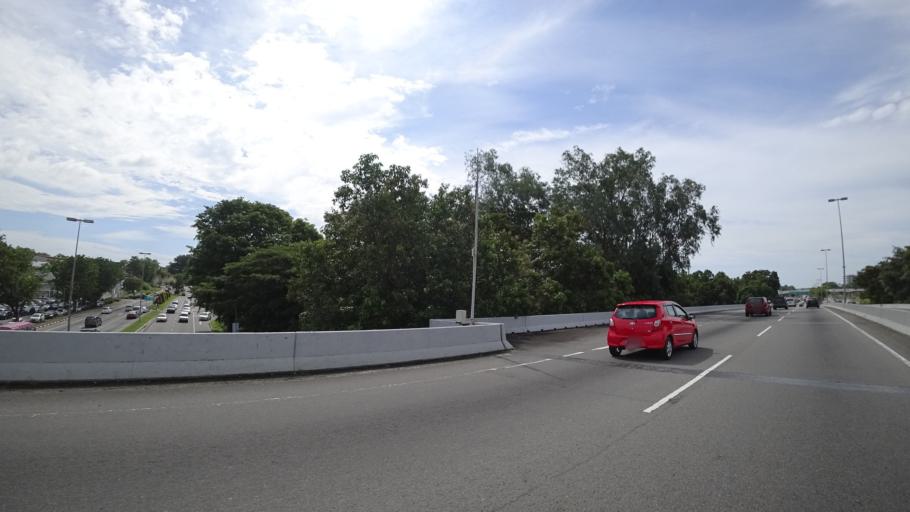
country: BN
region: Brunei and Muara
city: Bandar Seri Begawan
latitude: 4.9098
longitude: 114.9209
